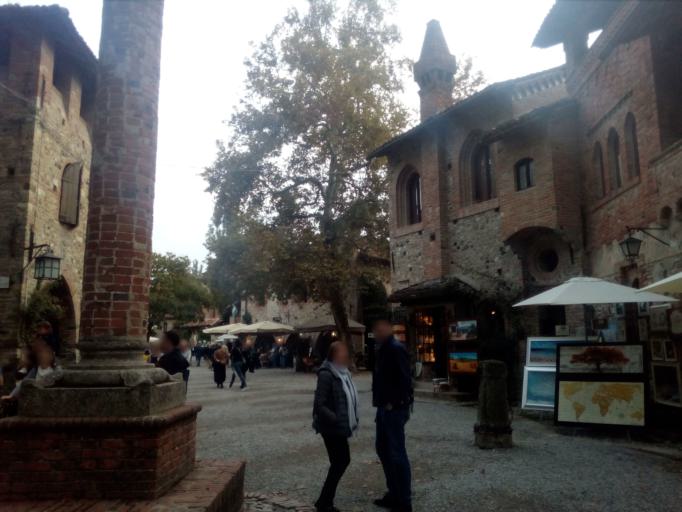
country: IT
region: Emilia-Romagna
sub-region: Provincia di Piacenza
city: Vigolzone
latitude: 44.9345
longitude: 9.6708
